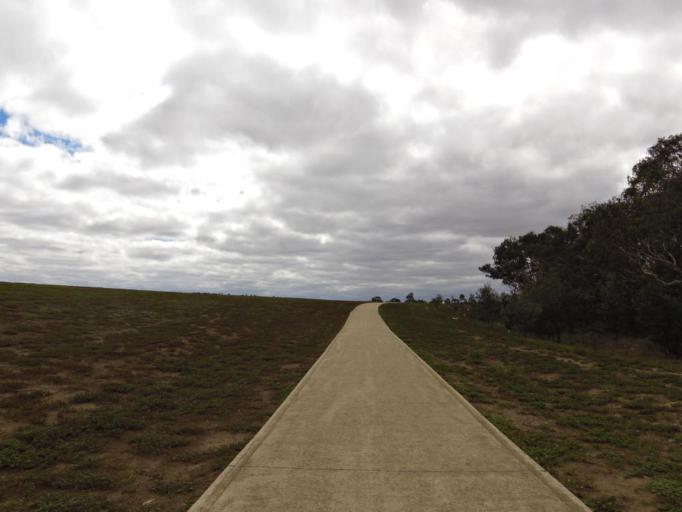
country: AU
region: Victoria
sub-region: Wyndham
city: Tarneit
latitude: -37.8827
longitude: 144.6399
